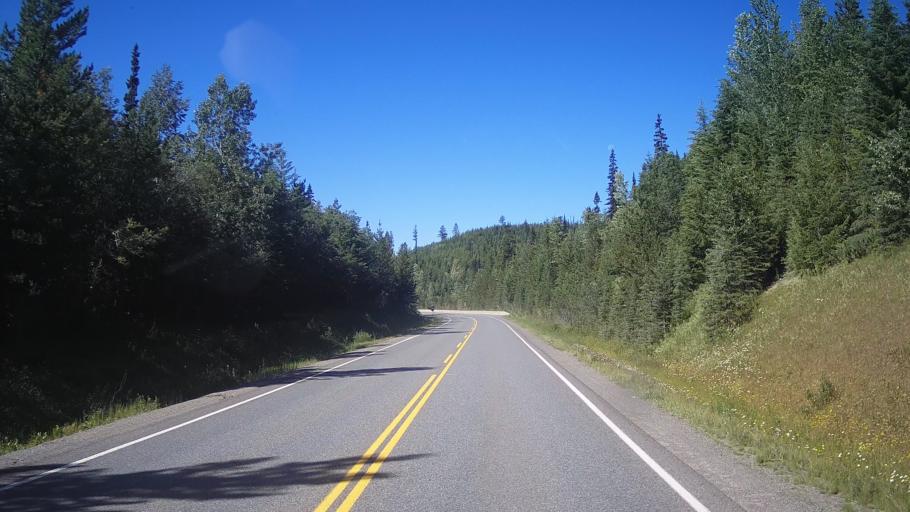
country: CA
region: British Columbia
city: Kamloops
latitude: 51.4980
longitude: -120.4475
